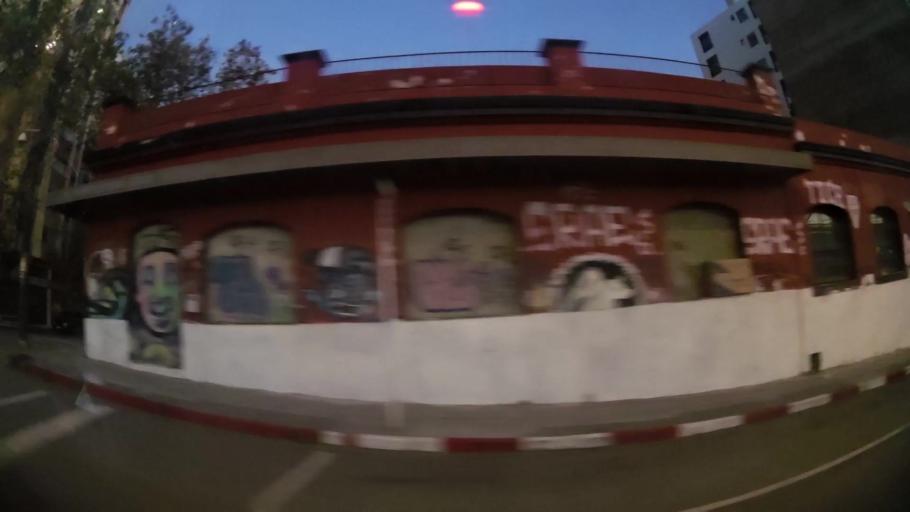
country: UY
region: Montevideo
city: Montevideo
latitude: -34.9085
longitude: -56.1999
